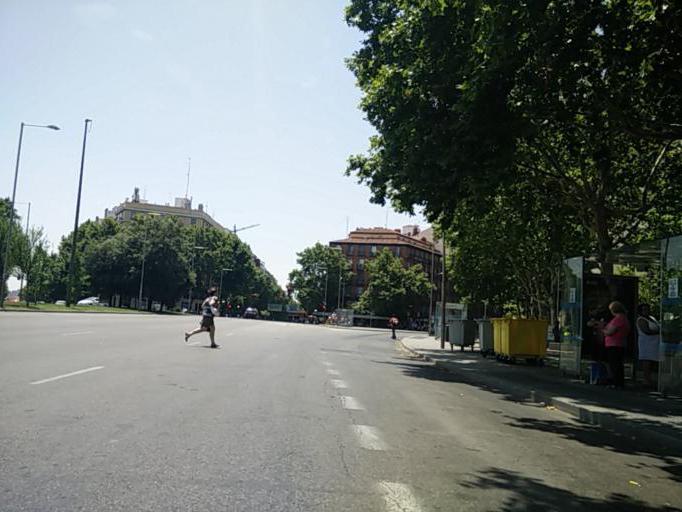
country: ES
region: Madrid
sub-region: Provincia de Madrid
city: Arganzuela
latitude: 40.4081
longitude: -3.6930
